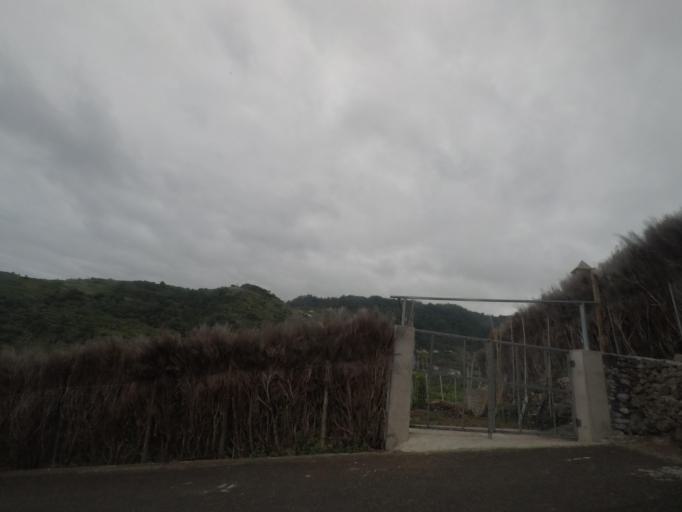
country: PT
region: Madeira
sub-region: Porto Moniz
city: Porto Moniz
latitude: 32.8551
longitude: -17.1594
